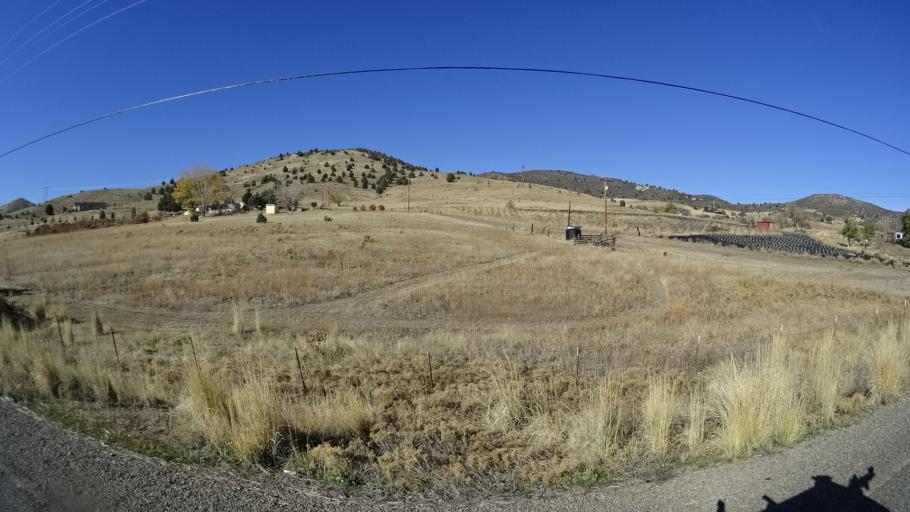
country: US
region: California
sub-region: Siskiyou County
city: Montague
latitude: 41.7911
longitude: -122.5145
